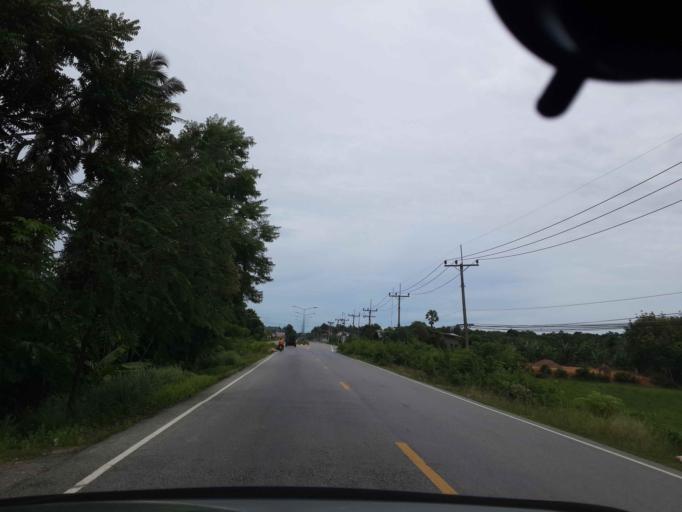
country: TH
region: Narathiwat
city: Yi-ngo
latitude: 6.3917
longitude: 101.6890
